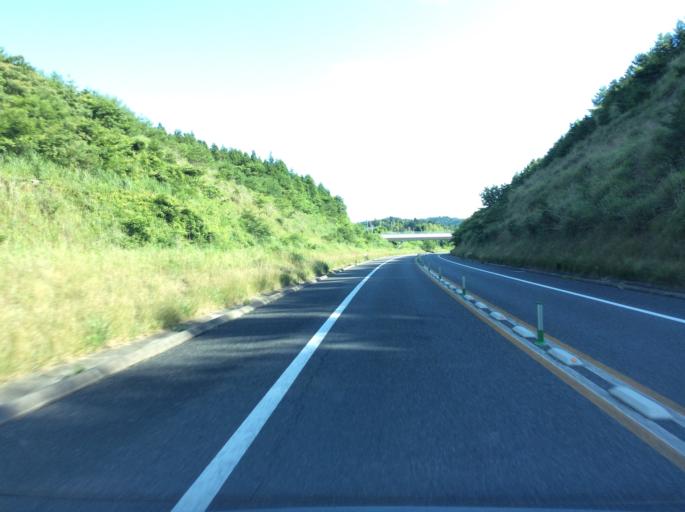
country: JP
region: Fukushima
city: Iwaki
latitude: 37.2211
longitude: 140.9767
